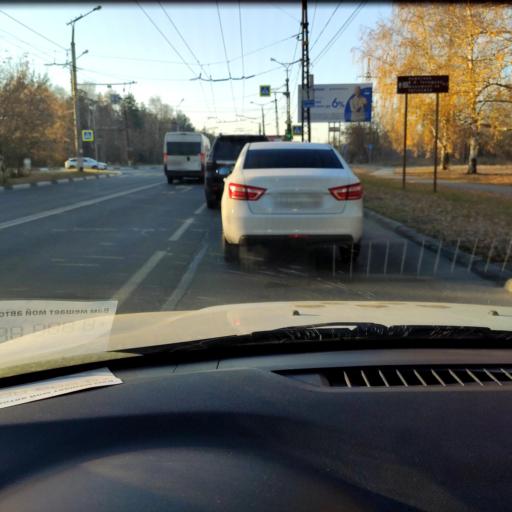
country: RU
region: Samara
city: Tol'yatti
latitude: 53.4996
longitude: 49.3891
